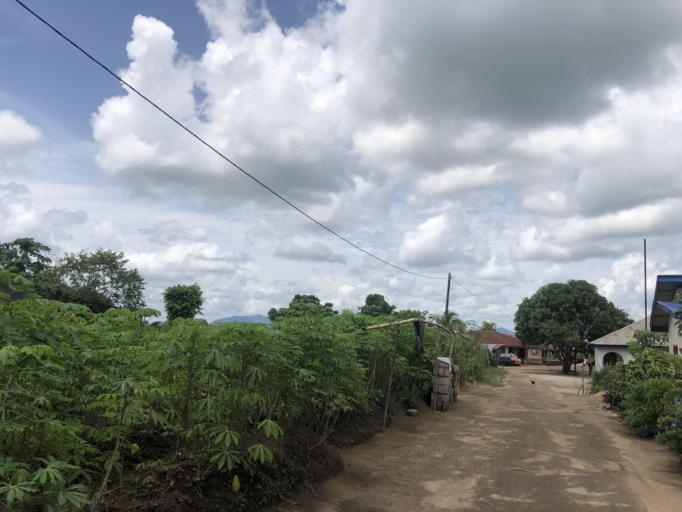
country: SL
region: Northern Province
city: Magburaka
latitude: 8.7138
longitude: -11.9266
